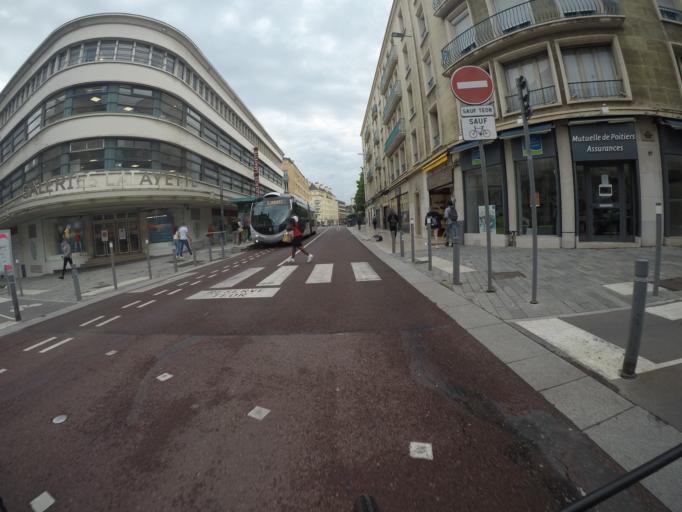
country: FR
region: Haute-Normandie
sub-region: Departement de la Seine-Maritime
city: Rouen
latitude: 49.4396
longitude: 1.0929
